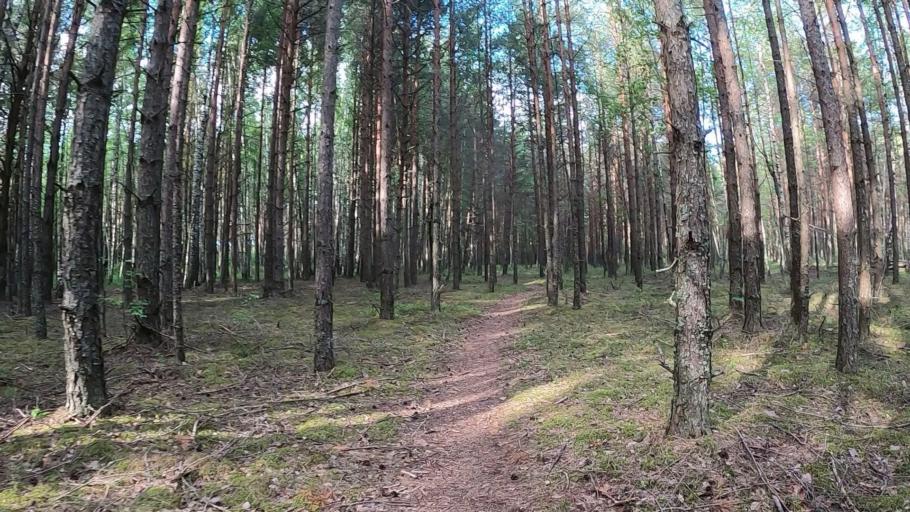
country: LV
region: Riga
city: Jaunciems
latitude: 57.0621
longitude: 24.1303
